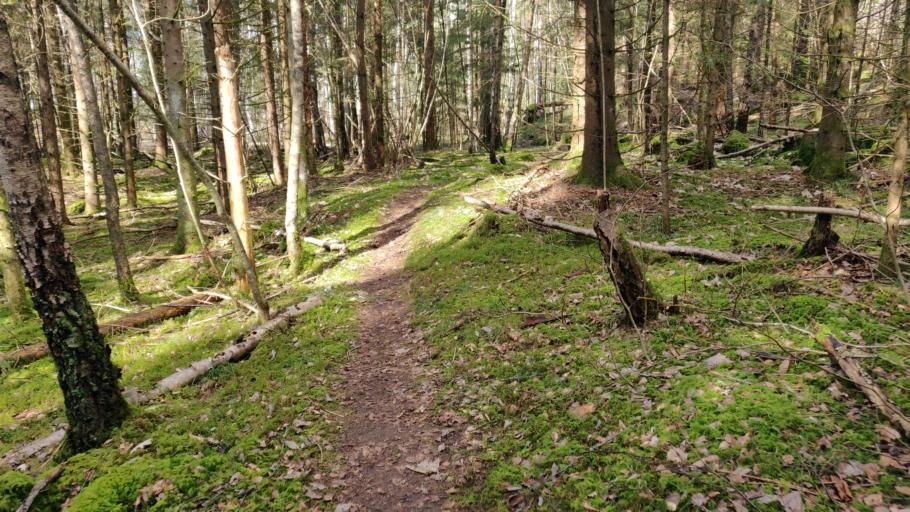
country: SE
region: Vaestra Goetaland
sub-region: Uddevalla Kommun
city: Uddevalla
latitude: 58.3412
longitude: 11.9349
